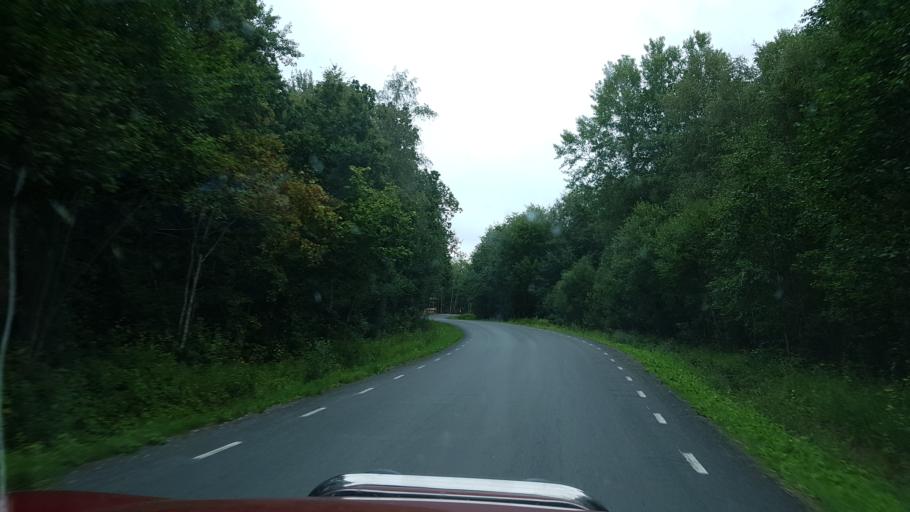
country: EE
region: Laeaene
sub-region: Lihula vald
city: Lihula
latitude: 58.8702
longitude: 23.9314
